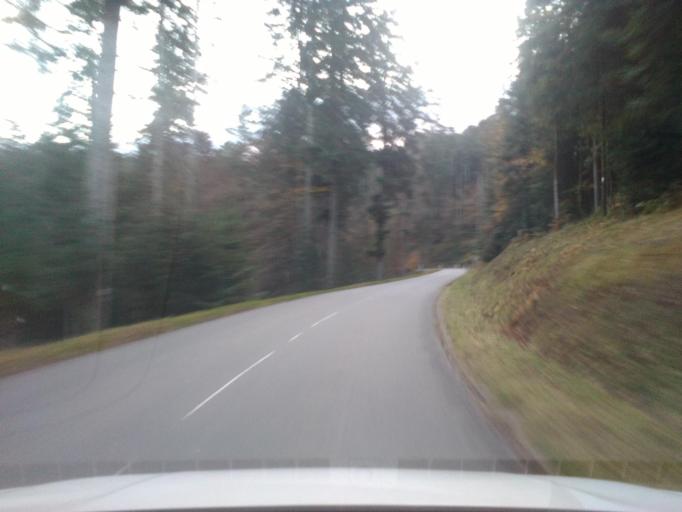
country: FR
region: Lorraine
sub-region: Departement des Vosges
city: Plainfaing
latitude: 48.2005
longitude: 7.0266
